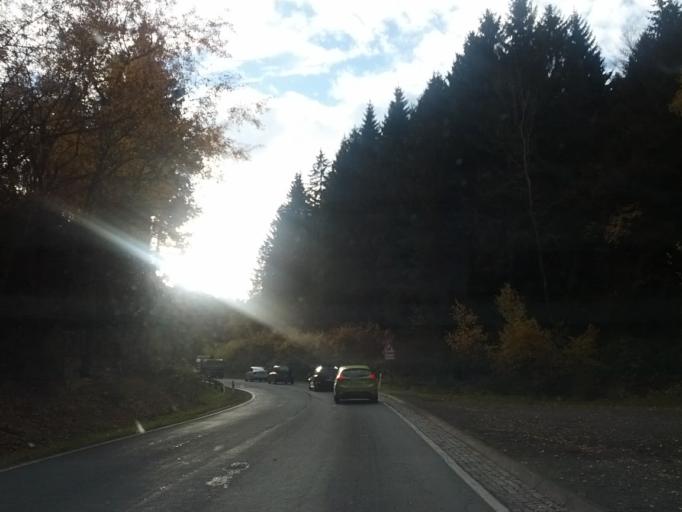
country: DE
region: Thuringia
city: Tabarz
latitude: 50.8670
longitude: 10.4876
